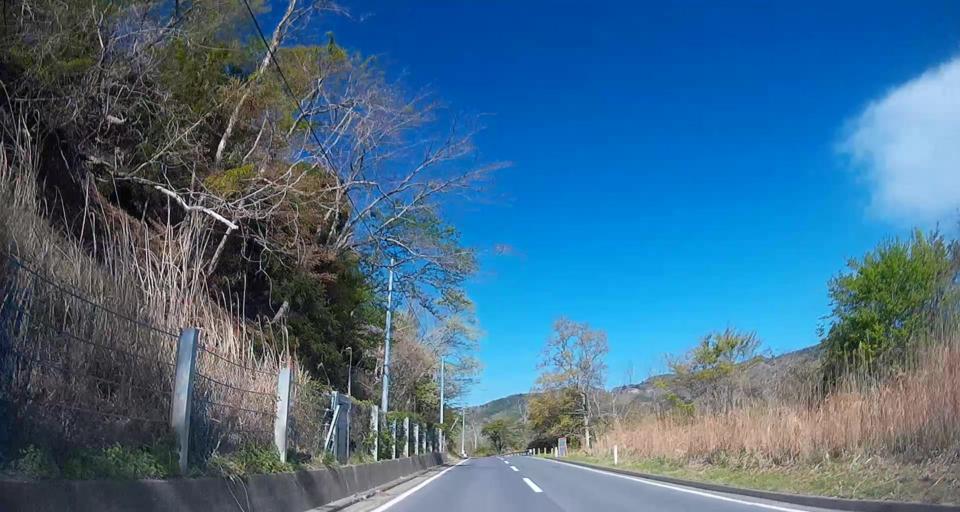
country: JP
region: Miyagi
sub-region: Oshika Gun
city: Onagawa Cho
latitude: 38.4368
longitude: 141.4404
